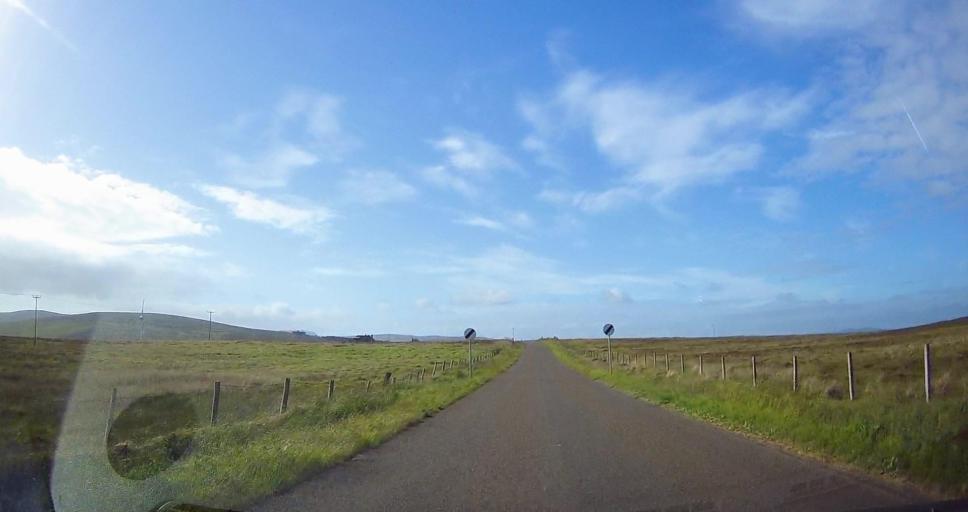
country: GB
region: Scotland
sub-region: Orkney Islands
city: Stromness
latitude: 58.8188
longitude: -3.2028
